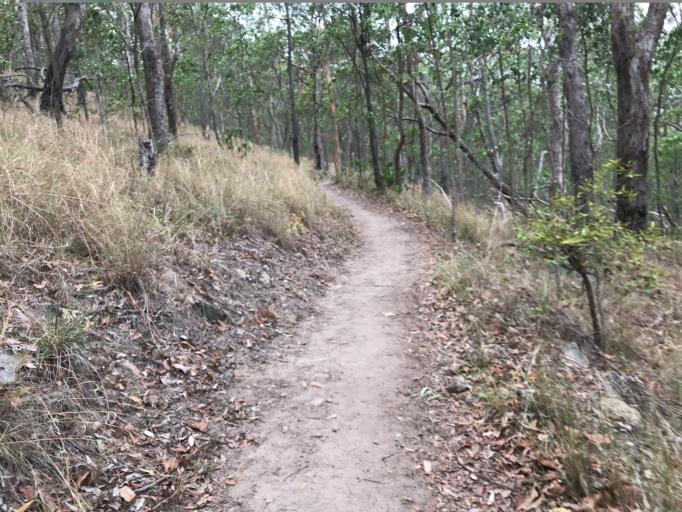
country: AU
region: Queensland
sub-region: Brisbane
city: Taringa
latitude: -27.4621
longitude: 152.9572
